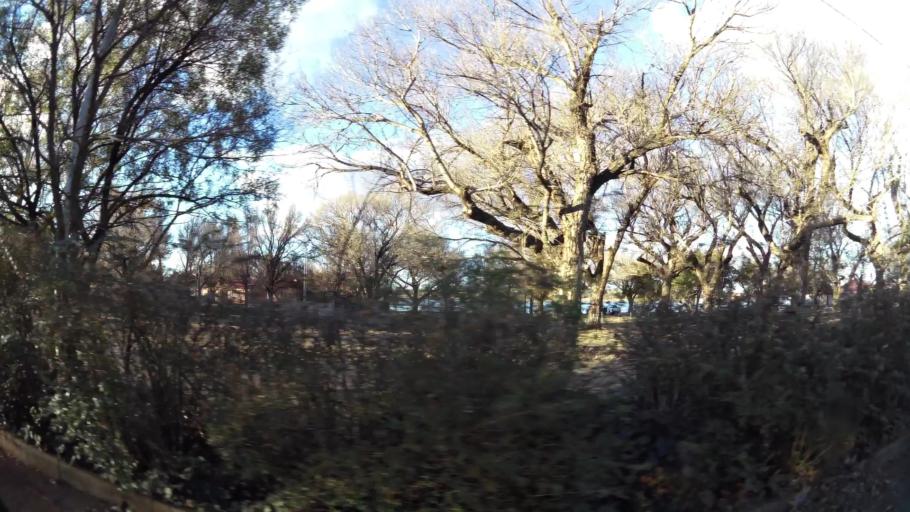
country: ZA
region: North-West
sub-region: Dr Kenneth Kaunda District Municipality
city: Potchefstroom
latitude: -26.6720
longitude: 27.0928
